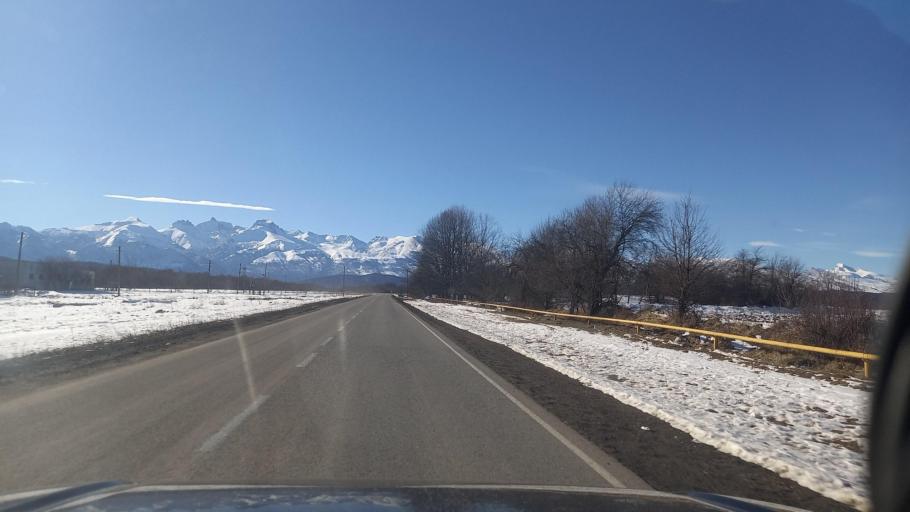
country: RU
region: North Ossetia
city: Chikola
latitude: 43.1719
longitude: 43.8695
